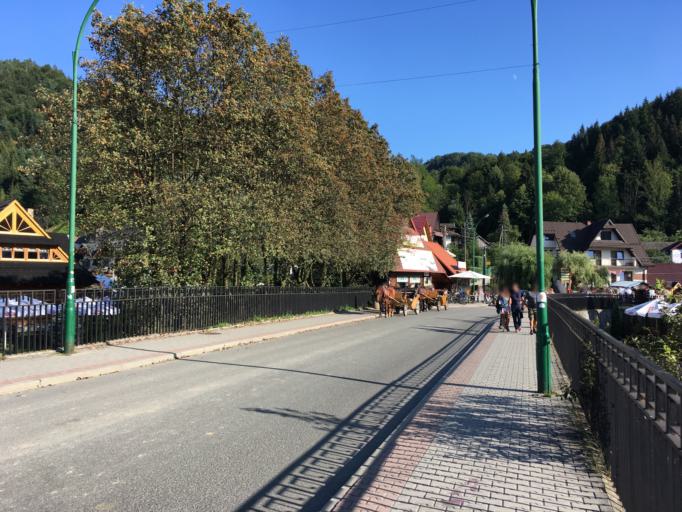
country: PL
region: Lesser Poland Voivodeship
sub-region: Powiat nowotarski
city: Szczawnica
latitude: 49.4239
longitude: 20.4599
